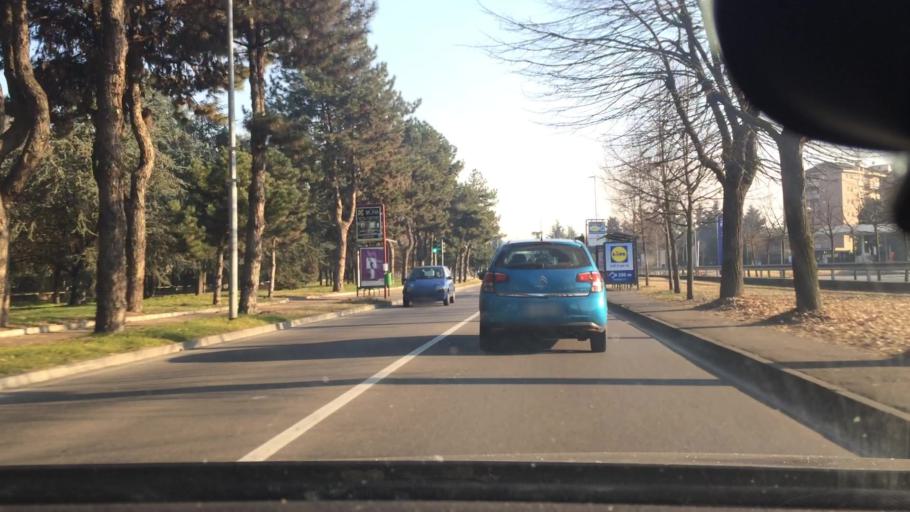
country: IT
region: Lombardy
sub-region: Citta metropolitana di Milano
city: Passirana
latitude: 45.5374
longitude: 9.0209
